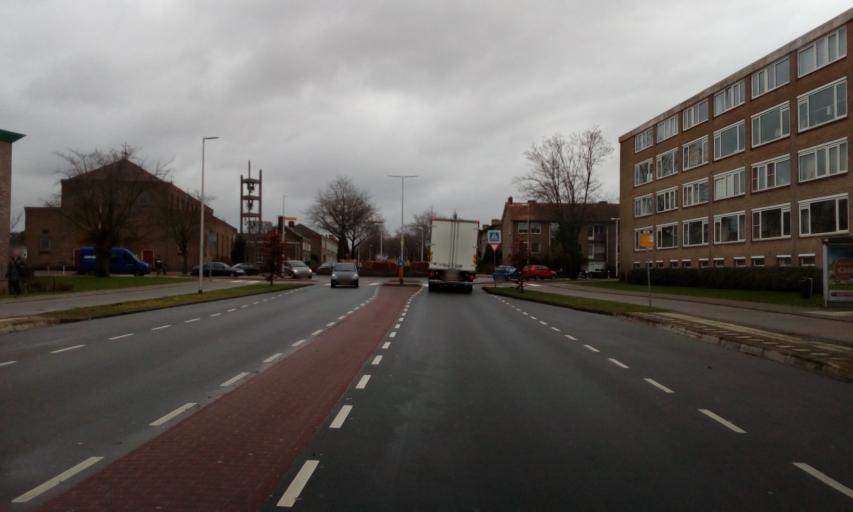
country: NL
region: North Holland
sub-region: Gemeente Bussum
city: Bussum
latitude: 52.2671
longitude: 5.1675
